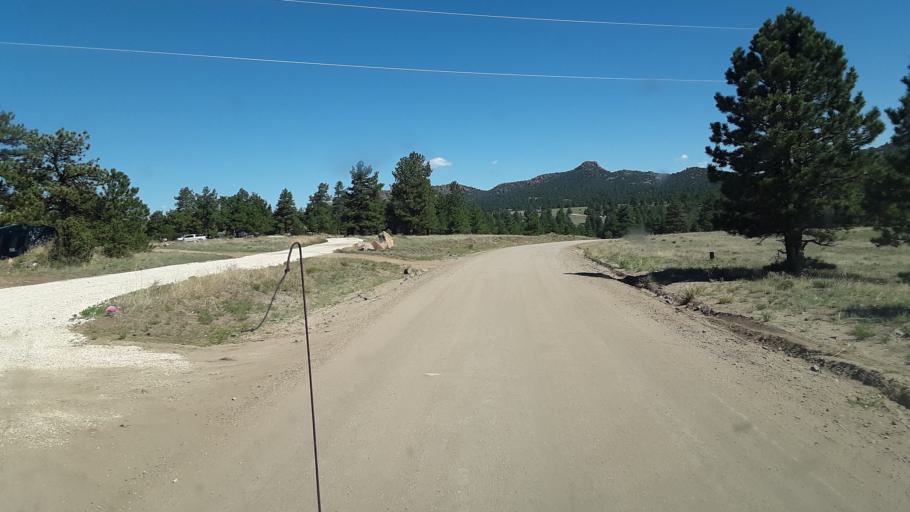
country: US
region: Colorado
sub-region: Custer County
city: Westcliffe
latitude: 38.2050
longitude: -105.4444
